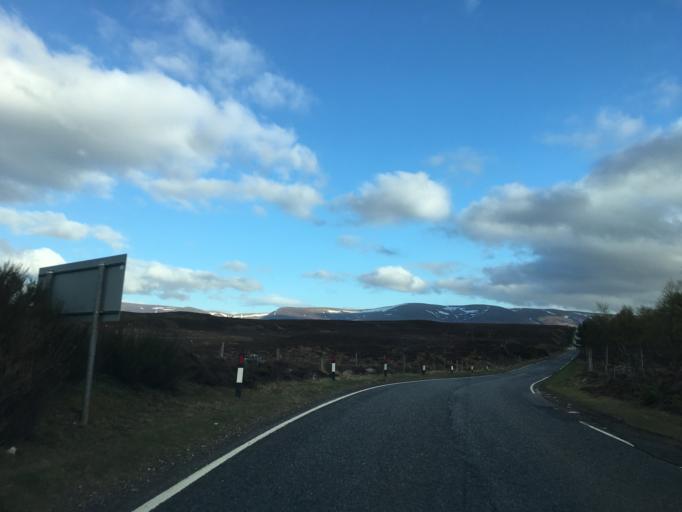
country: GB
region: Scotland
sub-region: Highland
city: Kingussie
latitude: 56.9839
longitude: -4.2383
